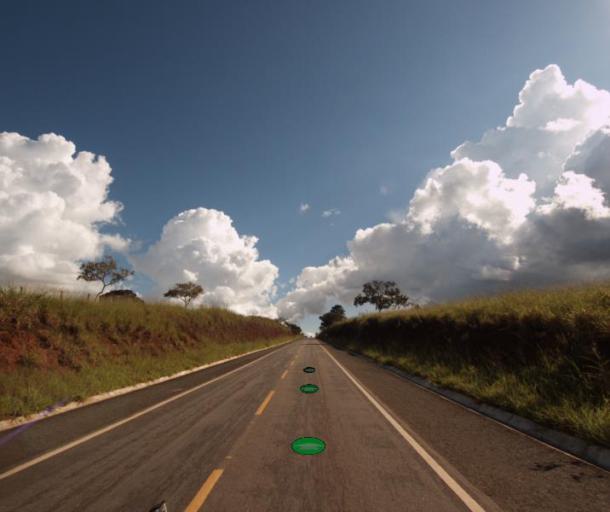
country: BR
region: Goias
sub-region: Itaberai
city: Itaberai
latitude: -15.9706
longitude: -49.6722
